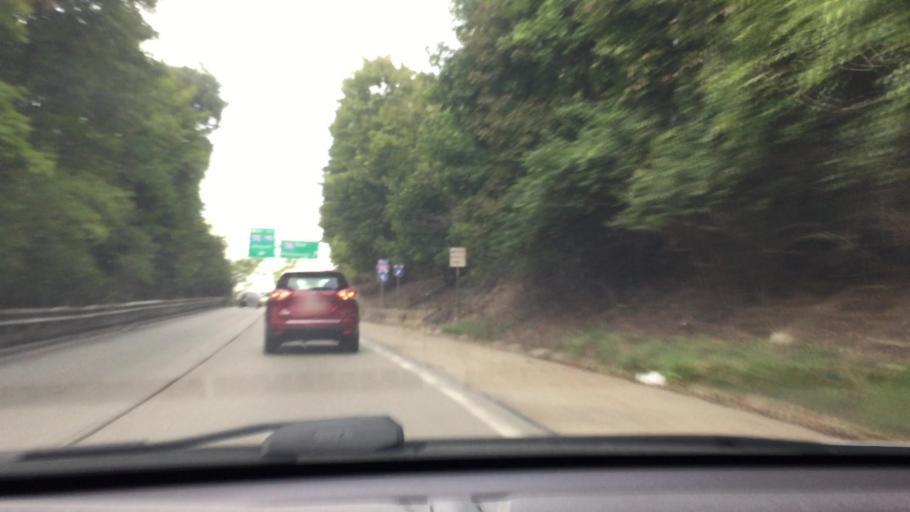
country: US
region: Pennsylvania
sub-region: Allegheny County
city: Carnegie
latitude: 40.4101
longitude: -80.0799
